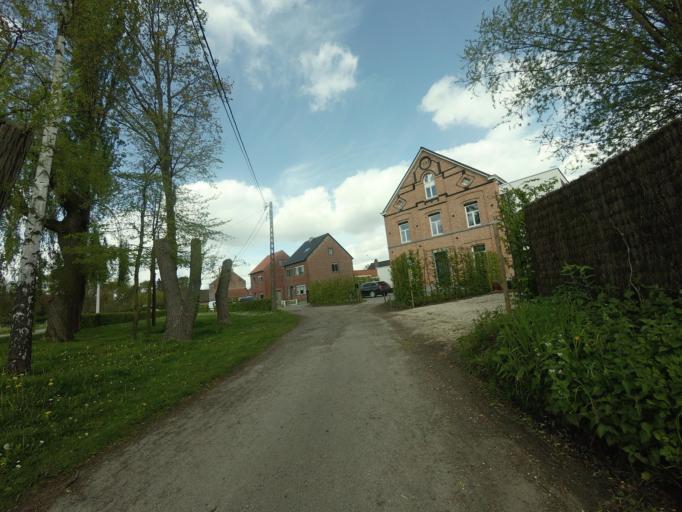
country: BE
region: Flanders
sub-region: Provincie Vlaams-Brabant
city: Kapelle-op-den-Bos
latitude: 51.0159
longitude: 4.4161
